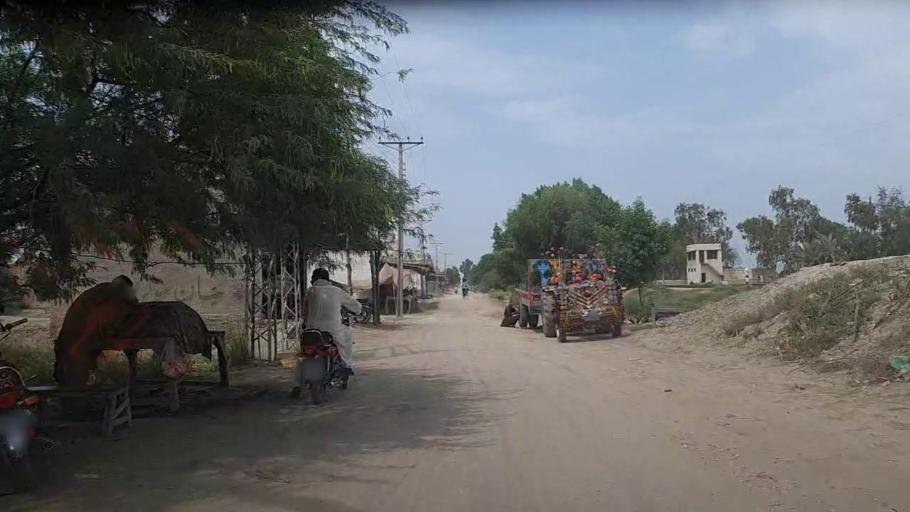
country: PK
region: Sindh
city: Bhiria
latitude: 26.8931
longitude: 68.2853
